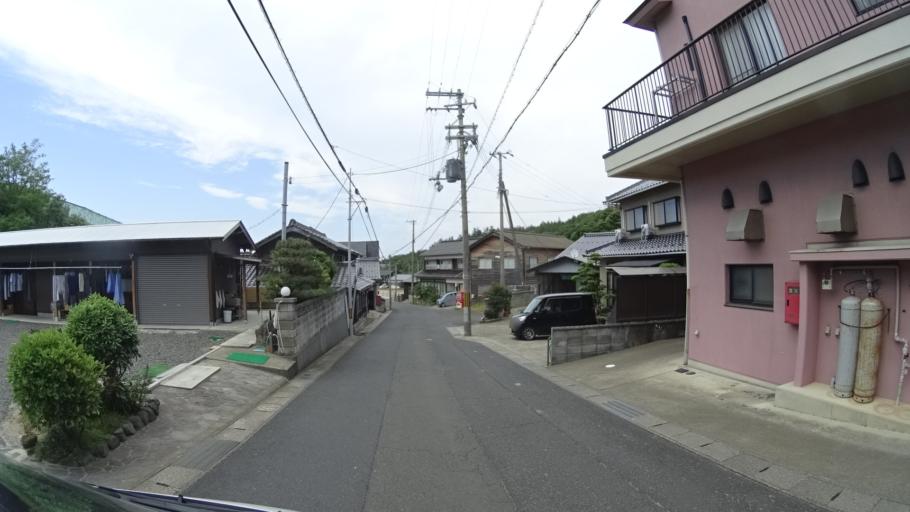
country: JP
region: Kyoto
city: Miyazu
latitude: 35.6981
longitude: 135.0548
